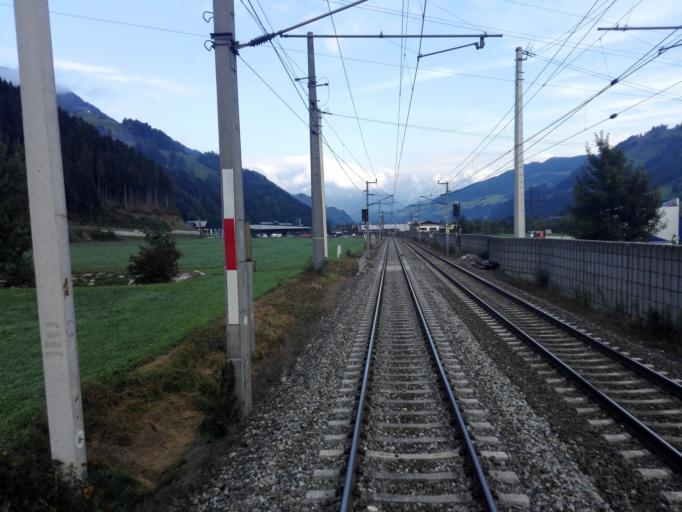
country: AT
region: Salzburg
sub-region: Politischer Bezirk Sankt Johann im Pongau
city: Sankt Johann im Pongau
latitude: 47.3648
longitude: 13.2054
